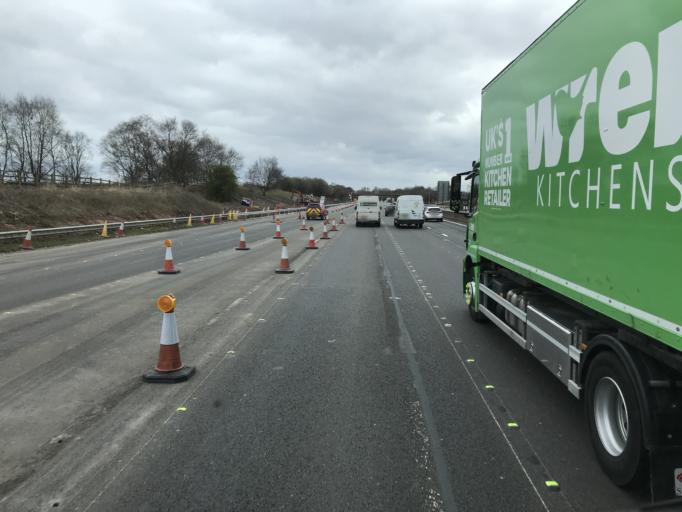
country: GB
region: England
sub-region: Warrington
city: Culcheth
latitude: 53.4359
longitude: -2.4949
